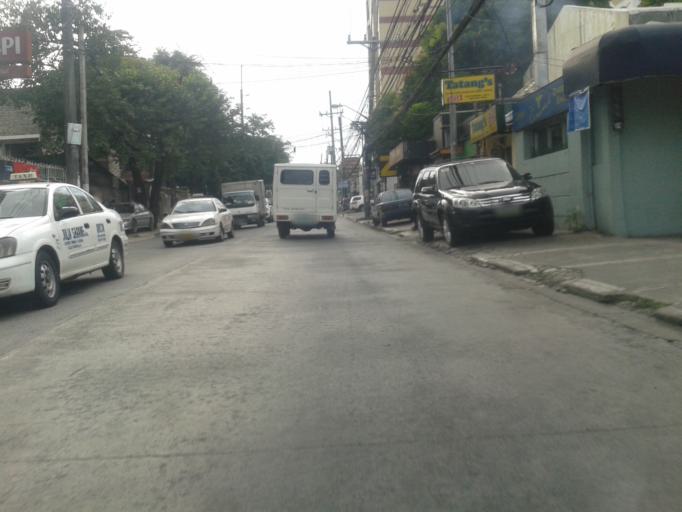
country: PH
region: Metro Manila
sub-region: Marikina
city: Calumpang
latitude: 14.6349
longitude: 121.0705
